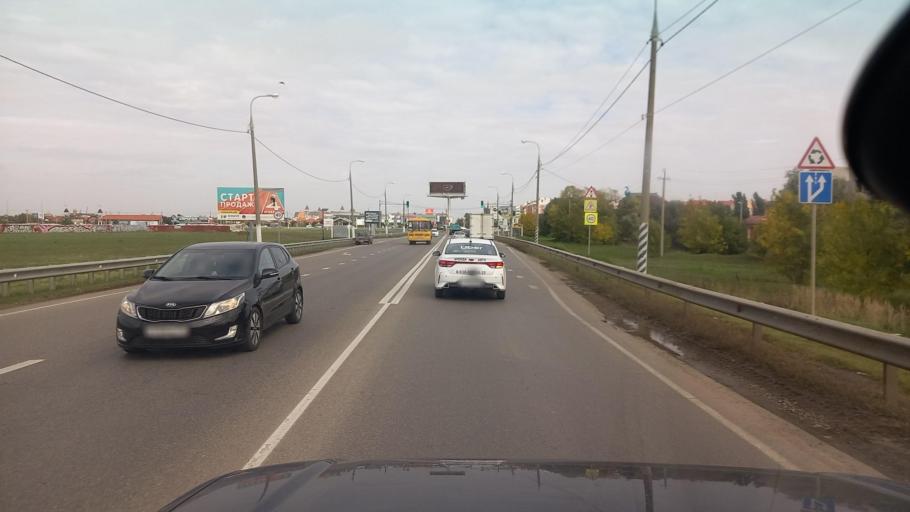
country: RU
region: Krasnodarskiy
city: Krasnodar
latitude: 45.1101
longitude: 38.9224
